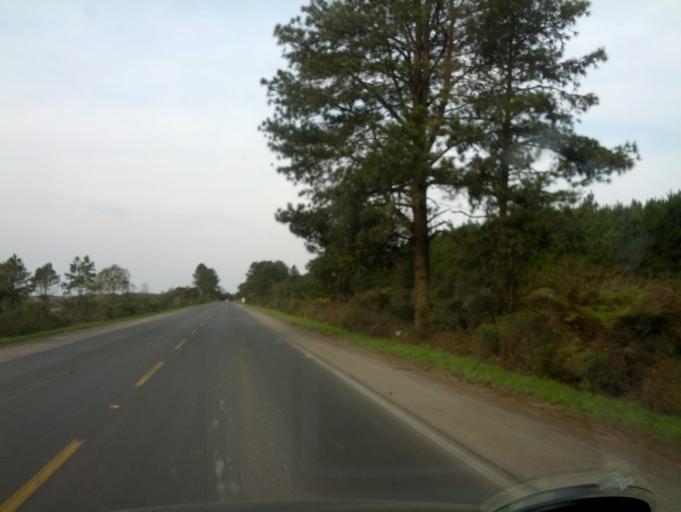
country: BR
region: Santa Catarina
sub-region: Otacilio Costa
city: Otacilio Costa
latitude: -27.3087
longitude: -50.1160
